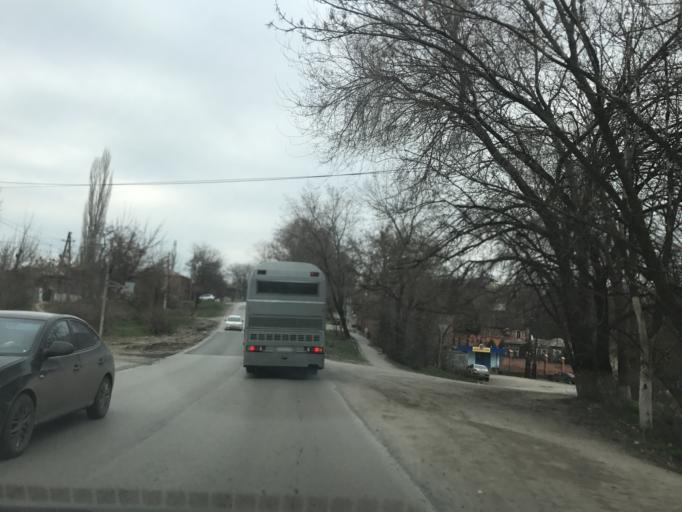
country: RU
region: Rostov
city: Novocherkassk
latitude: 47.4035
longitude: 40.0814
